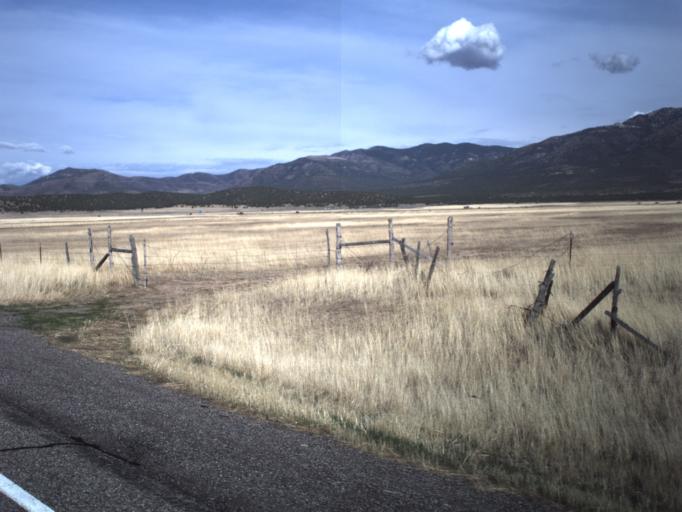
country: US
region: Utah
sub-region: Millard County
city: Fillmore
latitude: 39.1193
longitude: -112.2598
